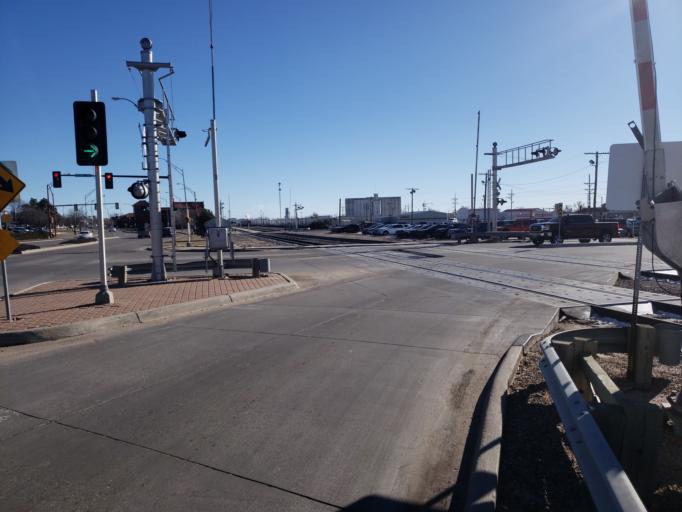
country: US
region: Kansas
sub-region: Ford County
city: Dodge City
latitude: 37.7525
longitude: -100.0196
